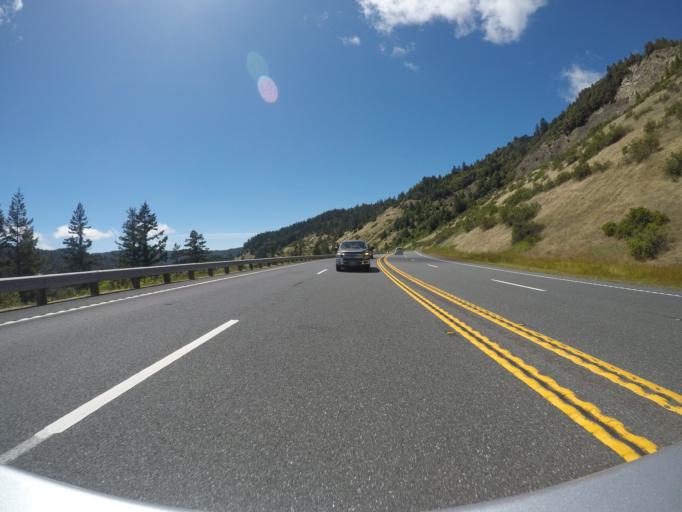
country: US
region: California
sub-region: Mendocino County
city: Laytonville
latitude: 39.8285
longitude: -123.6561
